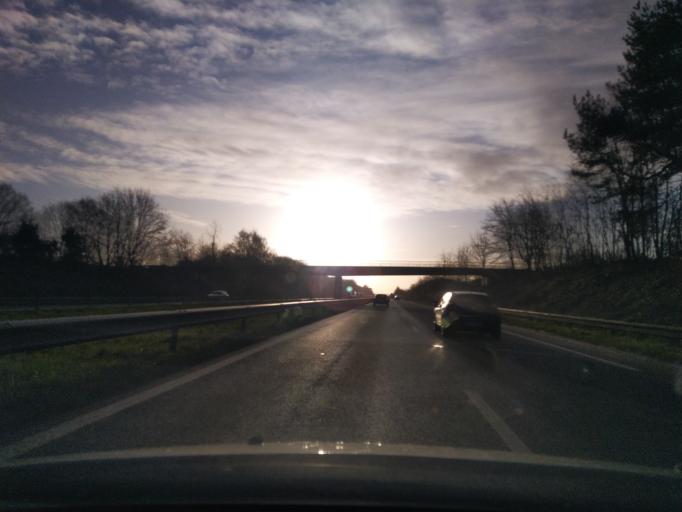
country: FR
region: Haute-Normandie
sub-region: Departement de la Seine-Maritime
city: Maromme
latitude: 49.4790
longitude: 1.0143
